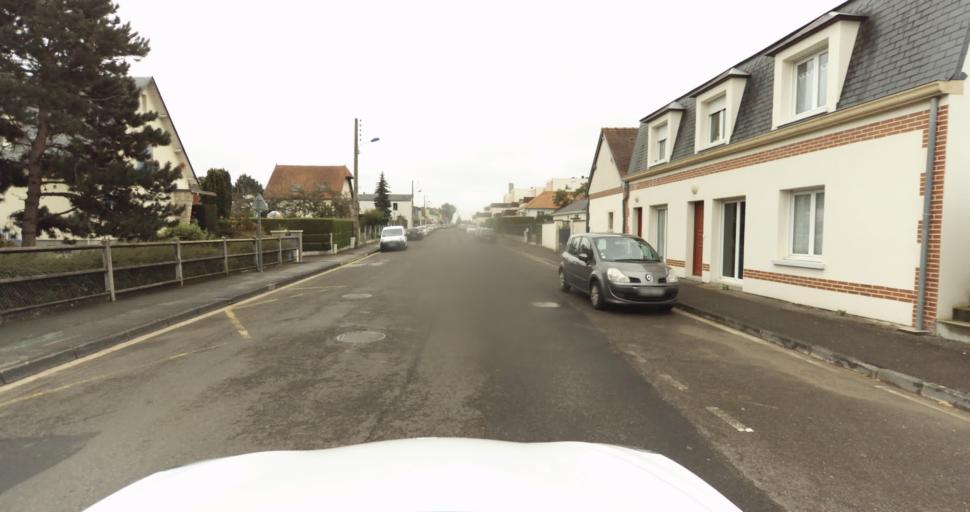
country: FR
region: Haute-Normandie
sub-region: Departement de l'Eure
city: Evreux
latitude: 49.0325
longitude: 1.1352
